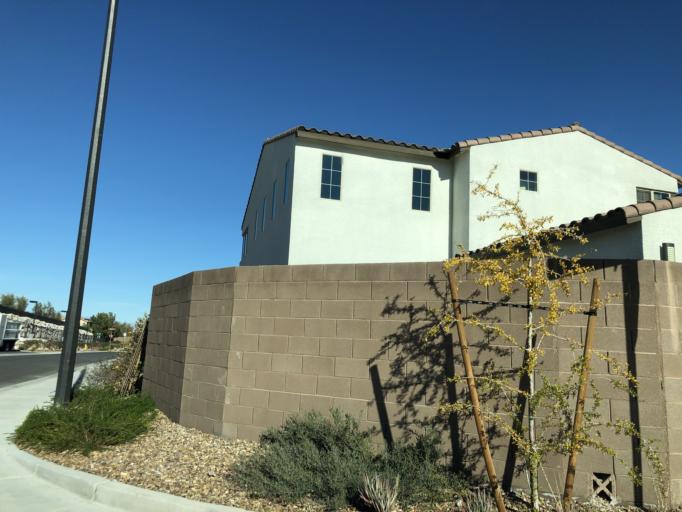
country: US
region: Nevada
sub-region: Clark County
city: Whitney
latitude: 35.9989
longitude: -115.0875
